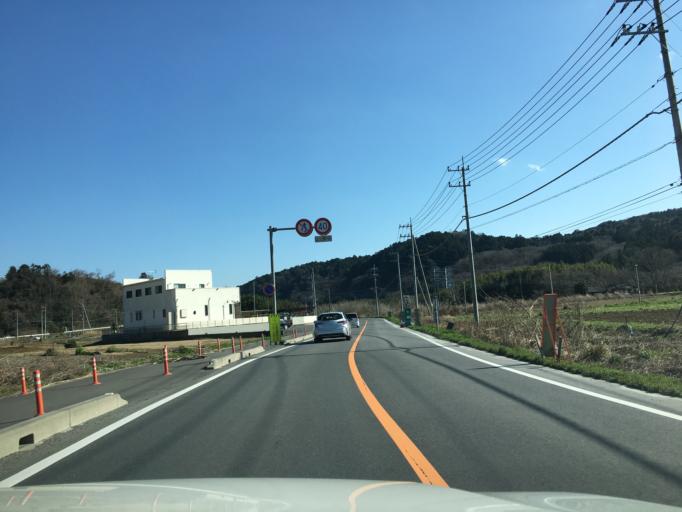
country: JP
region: Ibaraki
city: Omiya
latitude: 36.5561
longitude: 140.3190
